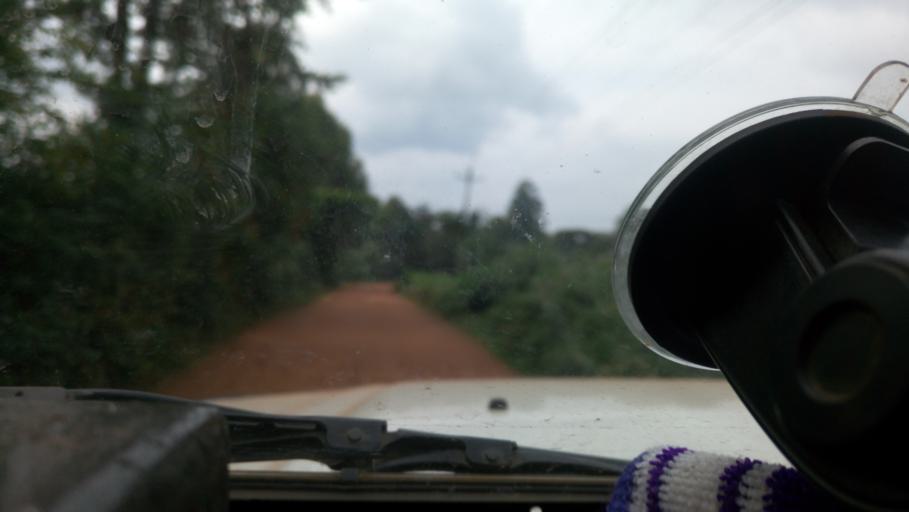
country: KE
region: Kericho
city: Litein
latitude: -0.5765
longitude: 35.2005
